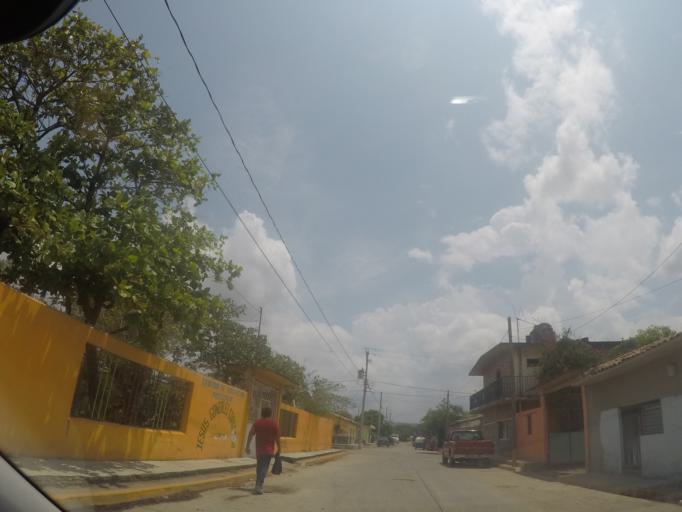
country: MX
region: Oaxaca
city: El Espinal
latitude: 16.5537
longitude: -94.9485
